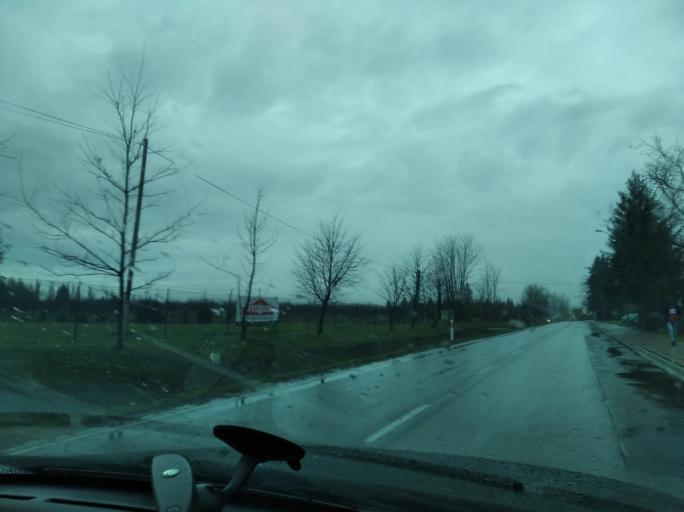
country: PL
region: Subcarpathian Voivodeship
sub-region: Powiat lancucki
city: Albigowa
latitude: 50.0273
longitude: 22.2265
